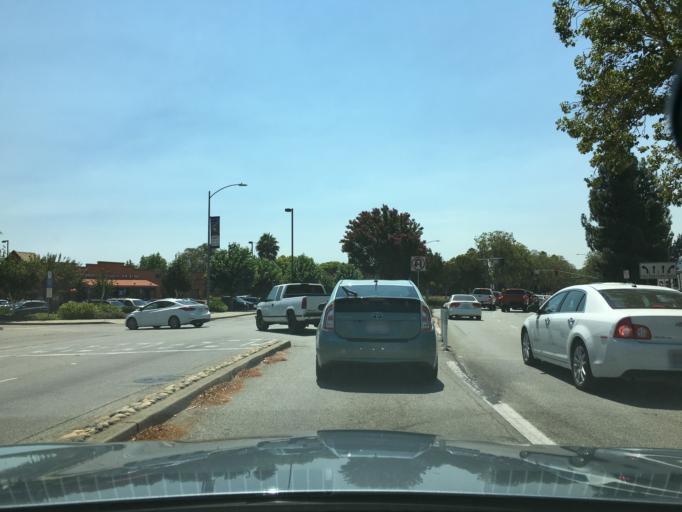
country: US
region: California
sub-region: Santa Clara County
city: Gilroy
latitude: 37.0221
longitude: -121.5624
